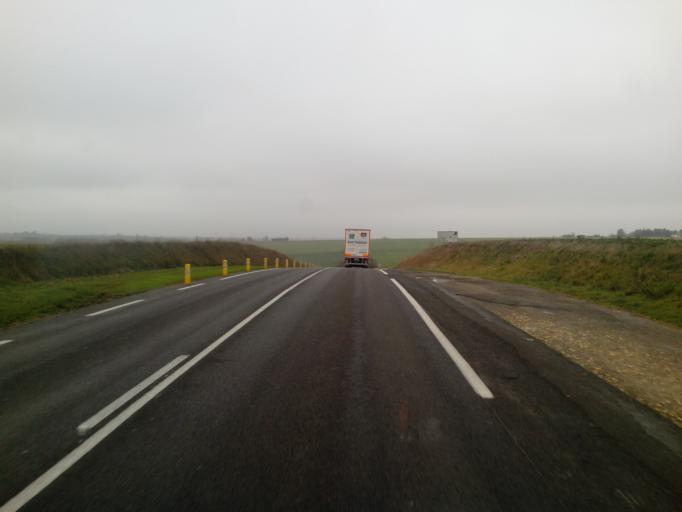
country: FR
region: Poitou-Charentes
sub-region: Departement de la Vienne
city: Cisse
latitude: 46.6354
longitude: 0.2252
